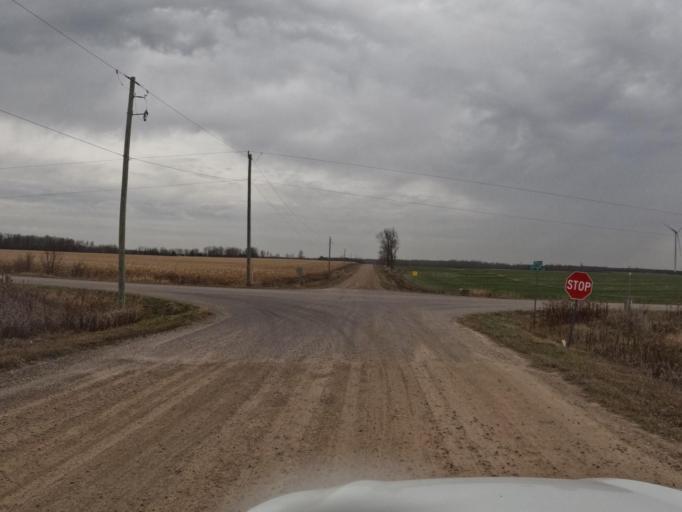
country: CA
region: Ontario
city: Shelburne
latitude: 43.8849
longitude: -80.3819
